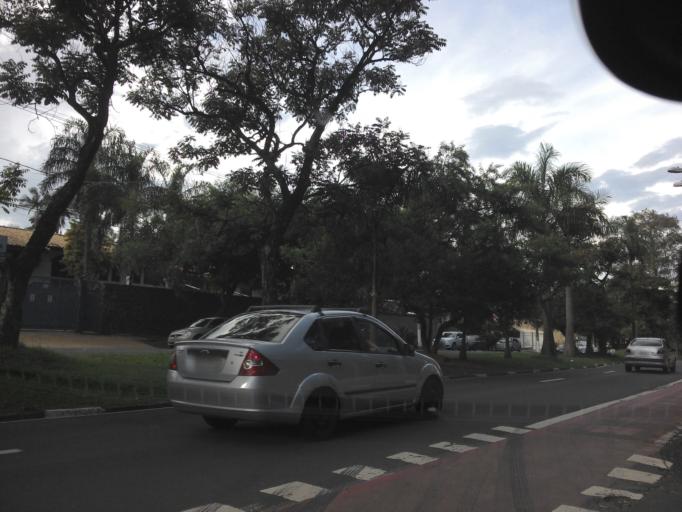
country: BR
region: Sao Paulo
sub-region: Campinas
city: Campinas
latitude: -22.8736
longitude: -47.0528
